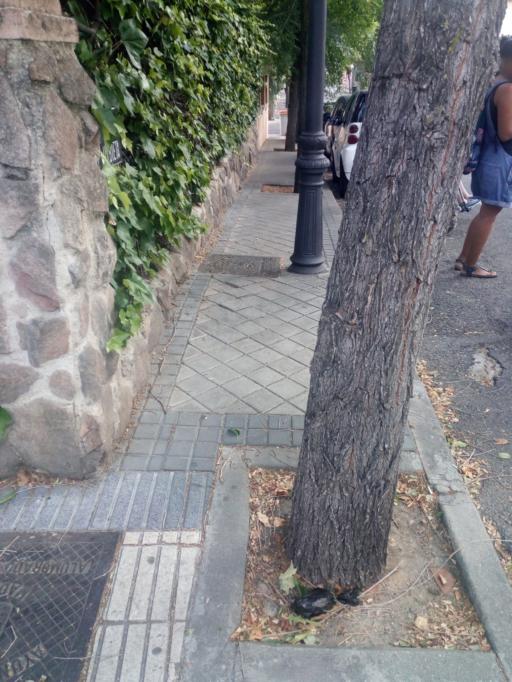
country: ES
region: Madrid
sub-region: Provincia de Madrid
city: Retiro
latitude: 40.4089
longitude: -3.6738
